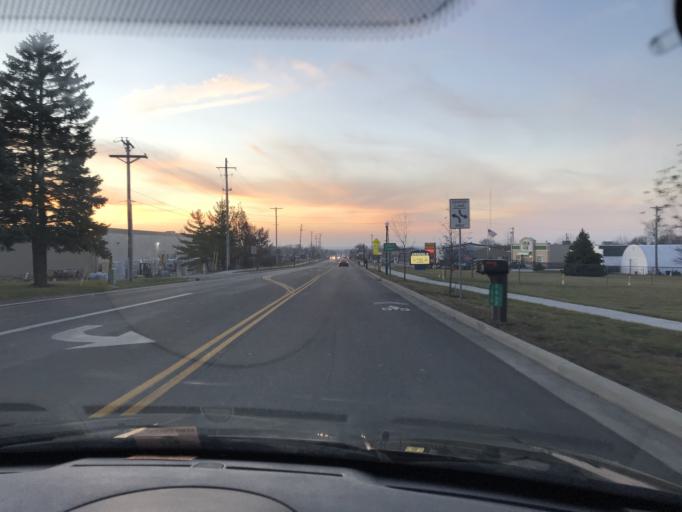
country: US
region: Ohio
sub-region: Champaign County
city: Urbana
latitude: 40.1060
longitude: -83.7185
